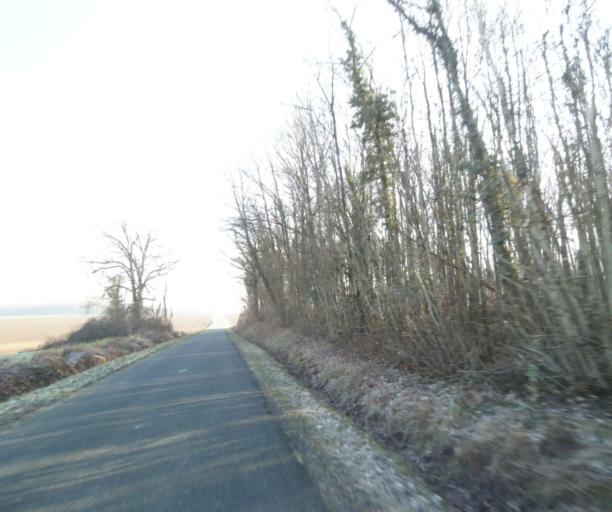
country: FR
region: Champagne-Ardenne
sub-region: Departement de la Haute-Marne
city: Chevillon
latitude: 48.4893
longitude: 5.0781
